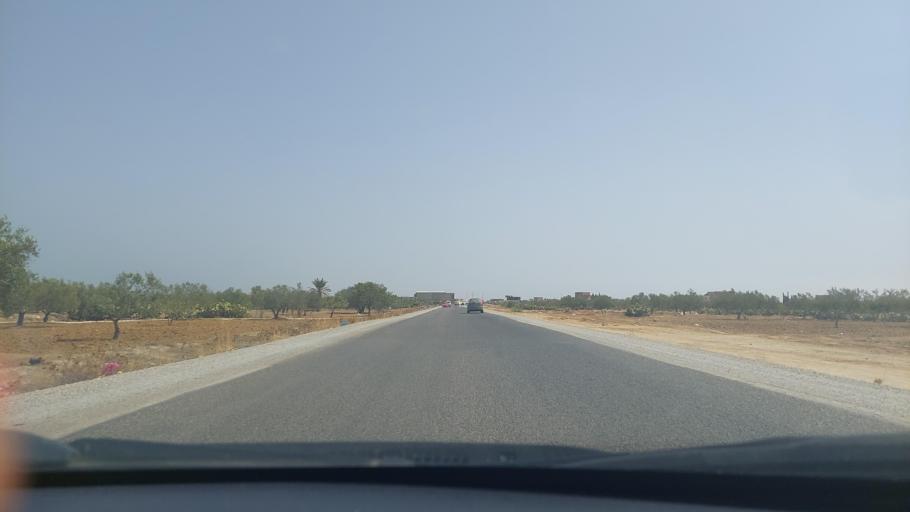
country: TN
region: Al Munastir
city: Qasr Hallal
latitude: 35.6050
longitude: 10.8837
